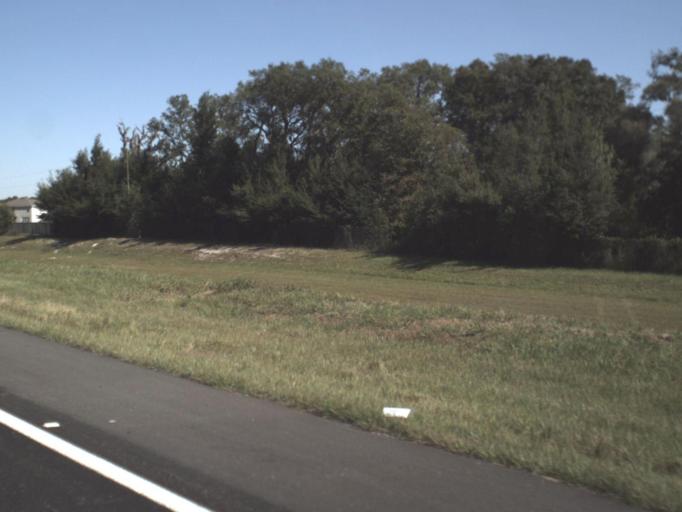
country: US
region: Florida
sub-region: Hernando County
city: Masaryktown
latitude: 28.4419
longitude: -82.4849
